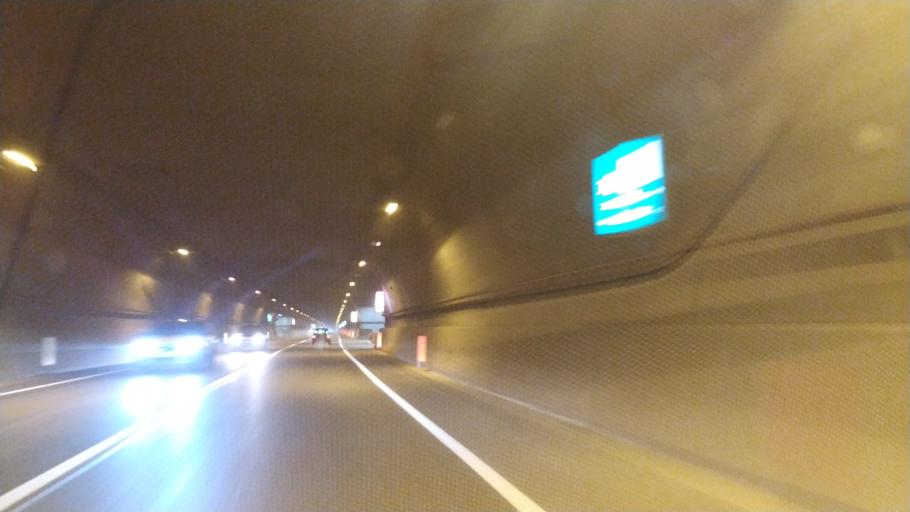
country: IT
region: Piedmont
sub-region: Provincia di Torino
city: Avigliana
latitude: 45.0642
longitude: 7.3965
